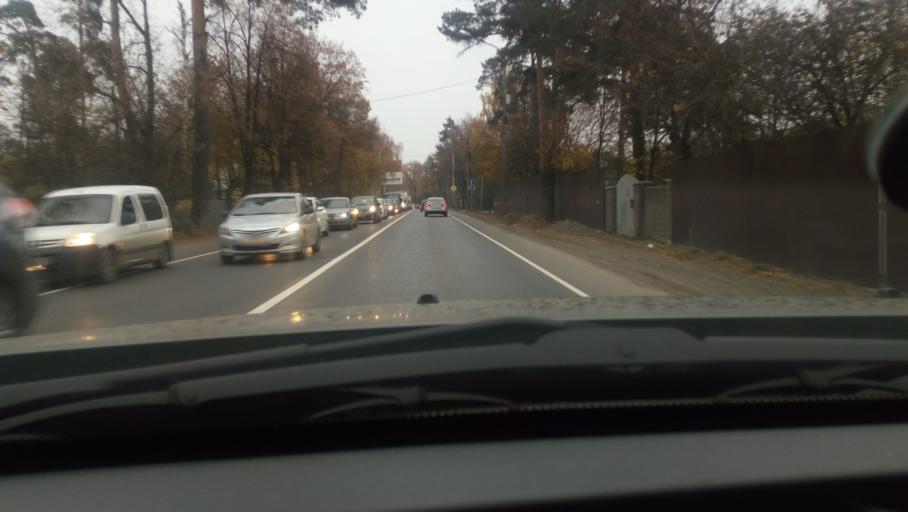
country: RU
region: Moskovskaya
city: Saltykovka
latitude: 55.7507
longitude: 37.9329
